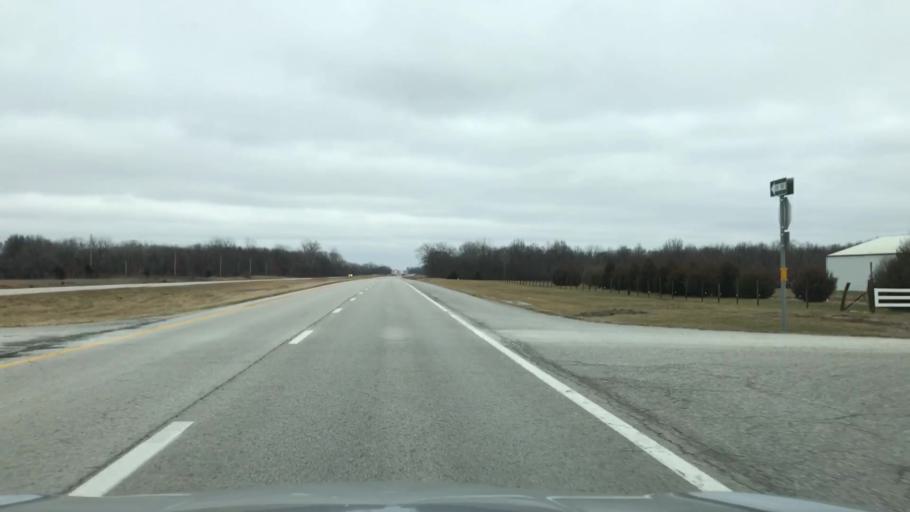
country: US
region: Missouri
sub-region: Livingston County
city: Chillicothe
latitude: 39.7767
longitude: -93.4444
